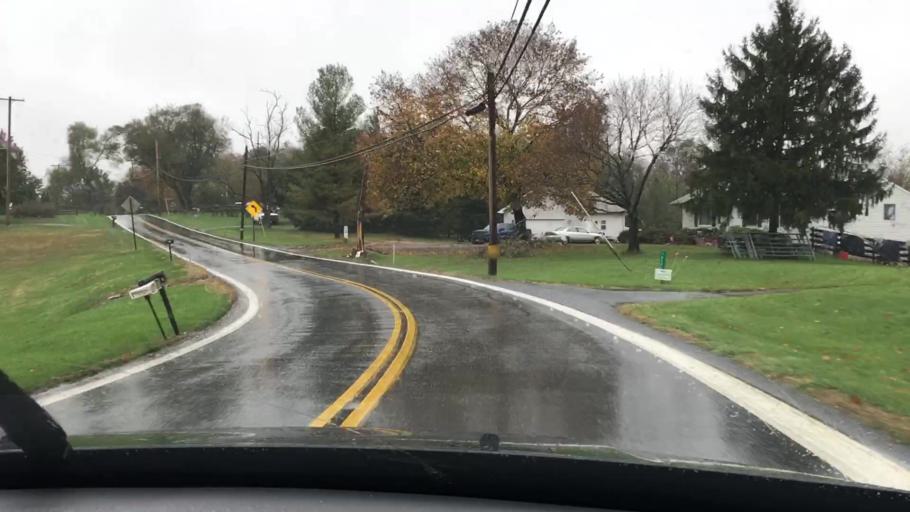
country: US
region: Maryland
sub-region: Frederick County
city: Buckeystown
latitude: 39.3341
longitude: -77.3924
